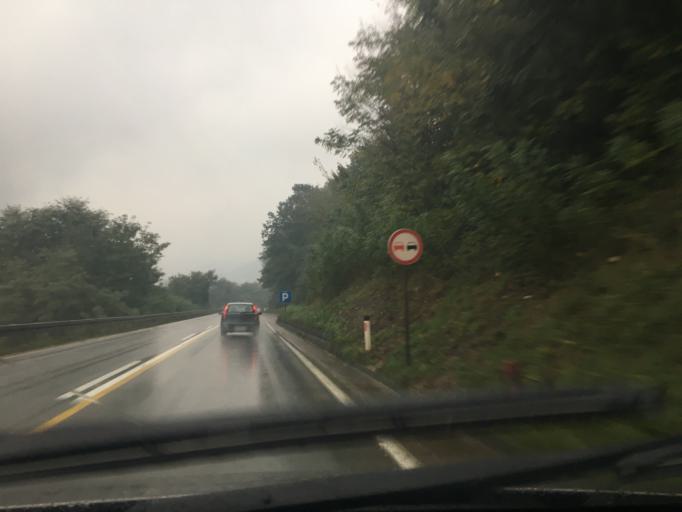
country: RS
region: Central Serbia
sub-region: Pcinjski Okrug
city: Vladicin Han
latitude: 42.8216
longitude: 22.1256
